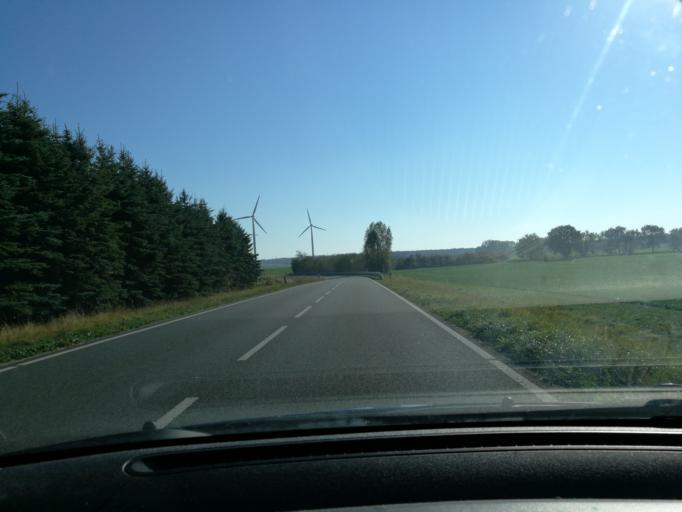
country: DE
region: Lower Saxony
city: Barendorf
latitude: 53.2242
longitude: 10.5160
